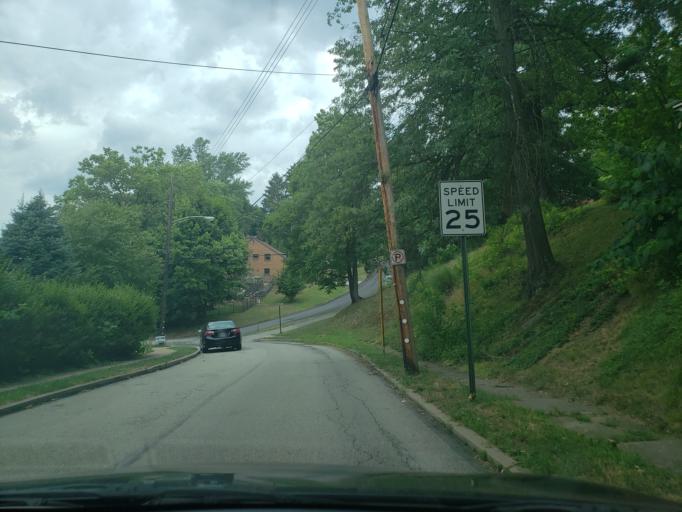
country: US
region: Pennsylvania
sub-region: Allegheny County
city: Ben Avon
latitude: 40.5100
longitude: -80.0830
